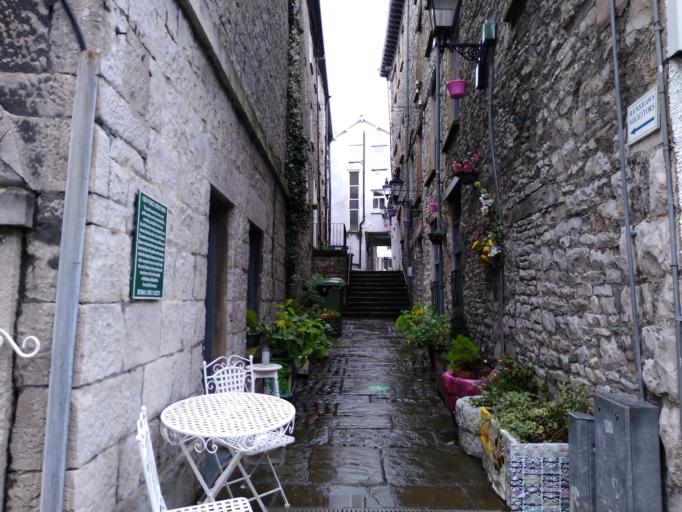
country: GB
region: England
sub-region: Cumbria
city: Kendal
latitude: 54.3280
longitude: -2.7460
